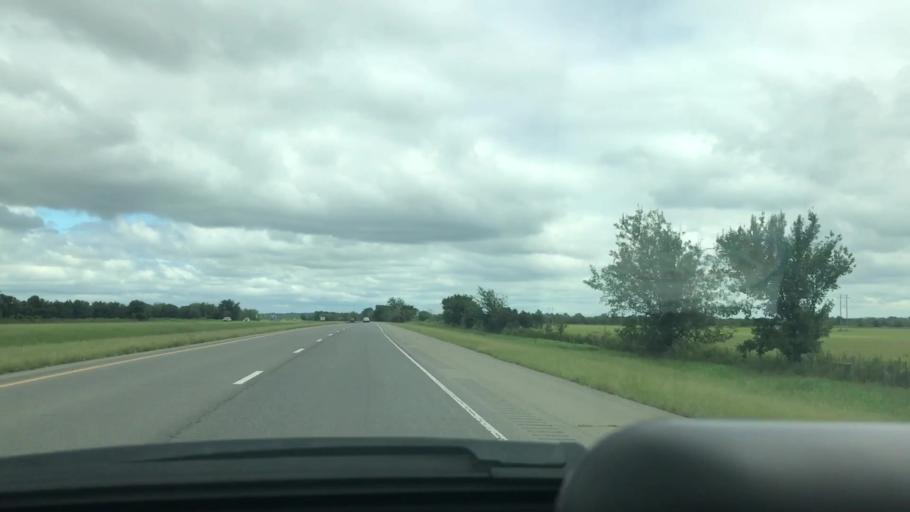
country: US
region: Oklahoma
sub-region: McIntosh County
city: Checotah
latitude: 35.5976
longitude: -95.4822
